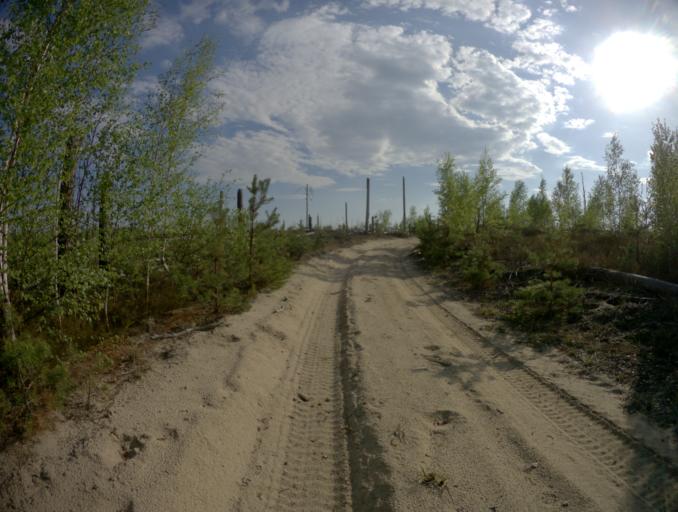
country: RU
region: Ivanovo
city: Talitsy
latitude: 56.4134
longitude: 42.2517
